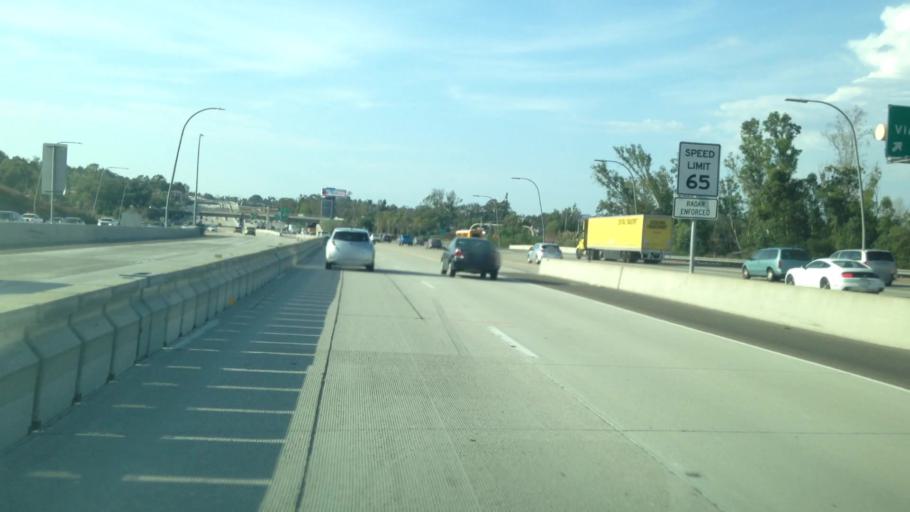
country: US
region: California
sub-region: San Diego County
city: Escondido
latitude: 33.0650
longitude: -117.0673
